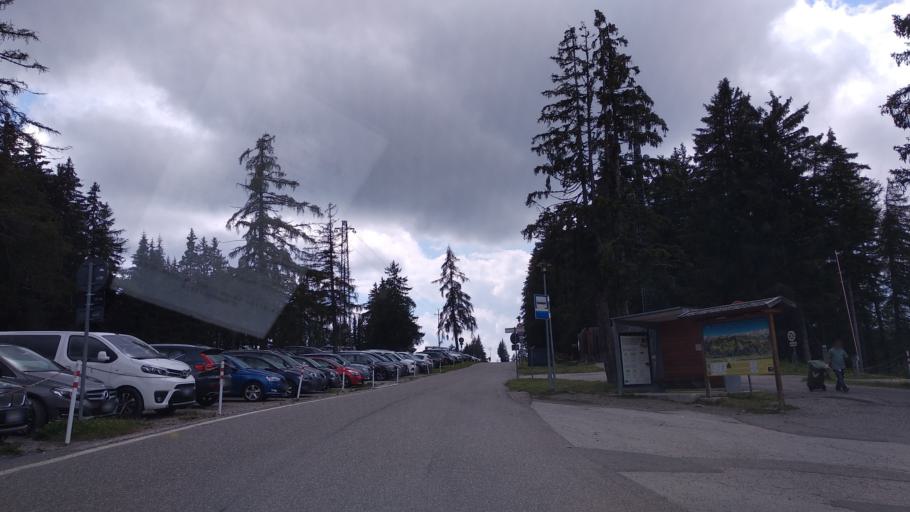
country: IT
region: Trentino-Alto Adige
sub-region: Bolzano
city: Avelengo
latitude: 46.6654
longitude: 11.2408
